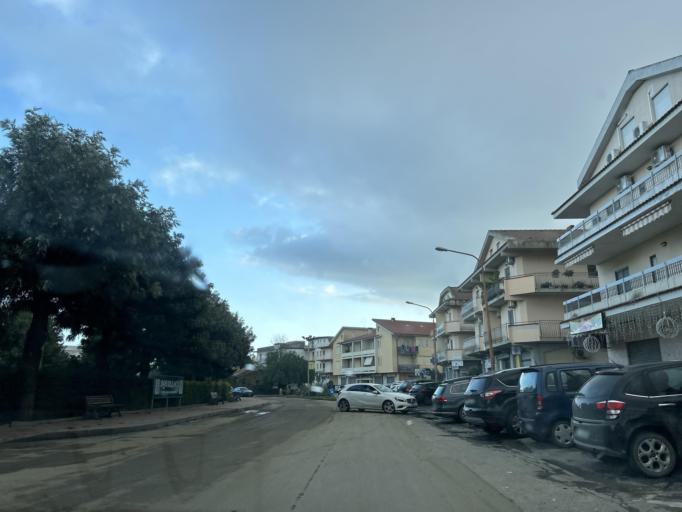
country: IT
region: Calabria
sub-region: Provincia di Catanzaro
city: Squillace Lido
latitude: 38.7784
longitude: 16.5692
